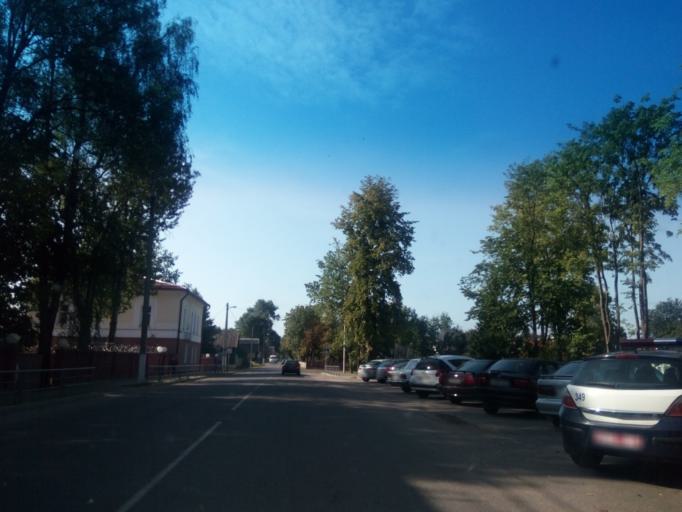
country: BY
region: Vitebsk
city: Vyerkhnyadzvinsk
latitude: 55.7760
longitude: 27.9320
